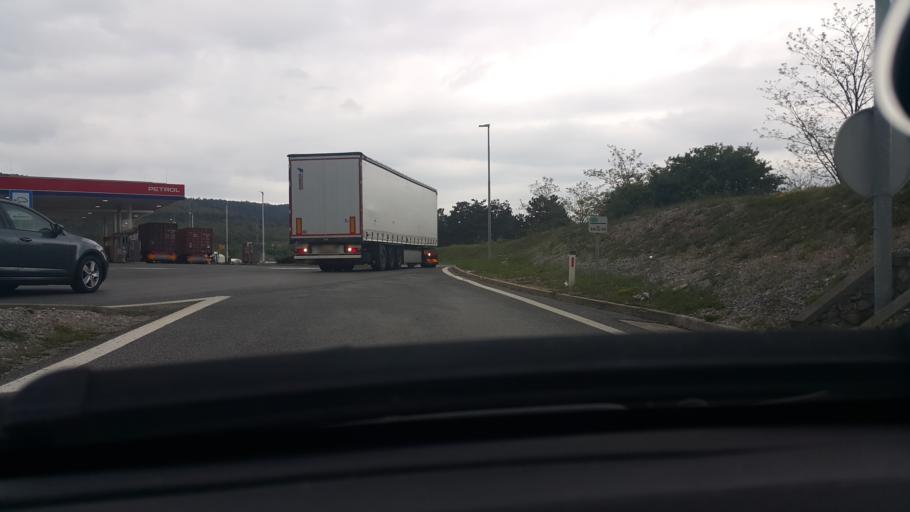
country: SI
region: Hrpelje-Kozina
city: Kozina
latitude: 45.6039
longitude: 13.9287
